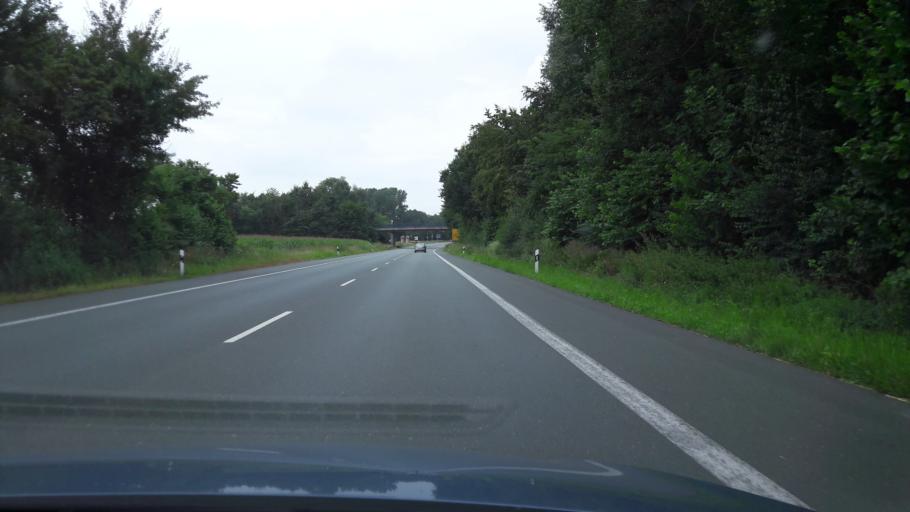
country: DE
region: North Rhine-Westphalia
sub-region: Regierungsbezirk Munster
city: Telgte
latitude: 51.9376
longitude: 7.7184
